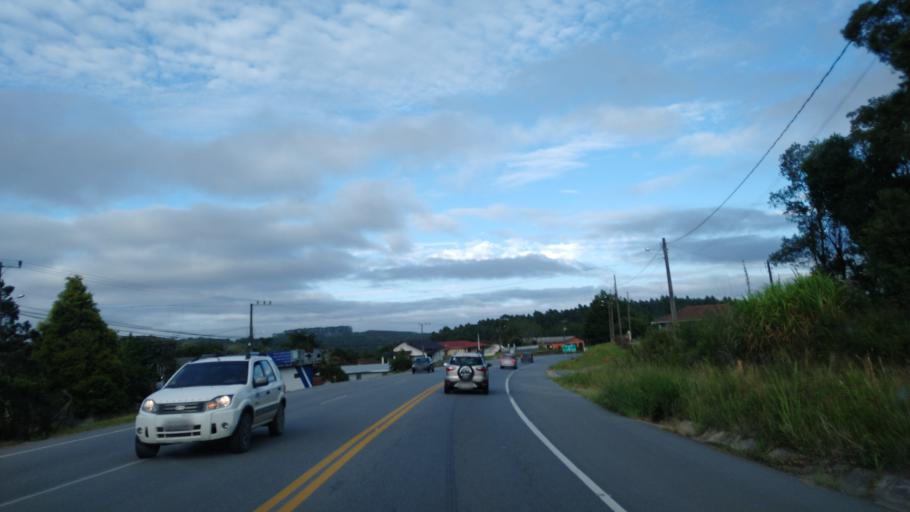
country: BR
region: Santa Catarina
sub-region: Sao Bento Do Sul
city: Sao Bento do Sul
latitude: -26.2464
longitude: -49.4484
